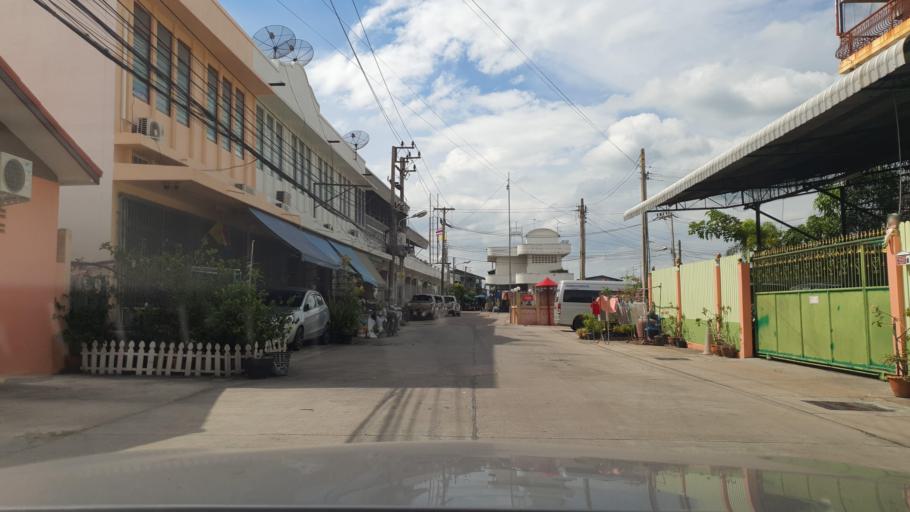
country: TH
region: Chon Buri
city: Chon Buri
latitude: 13.3698
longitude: 100.9791
